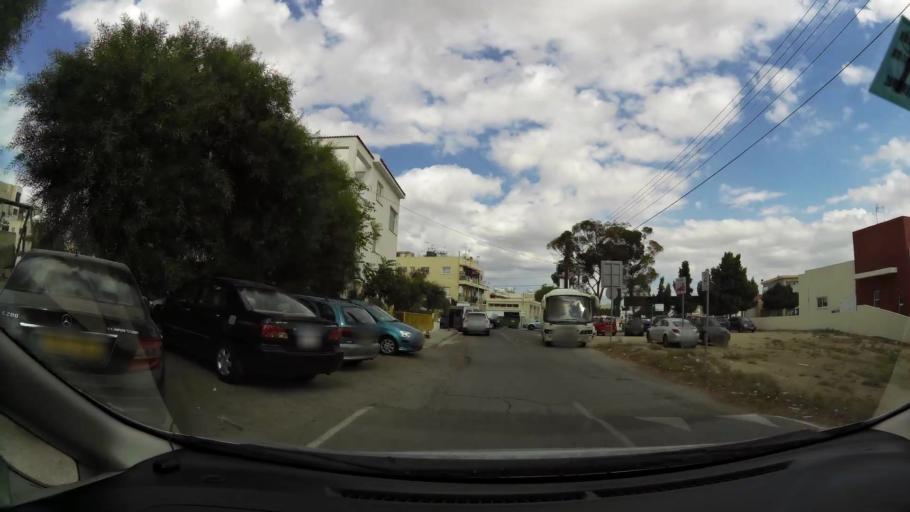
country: CY
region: Lefkosia
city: Nicosia
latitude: 35.1770
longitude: 33.3782
